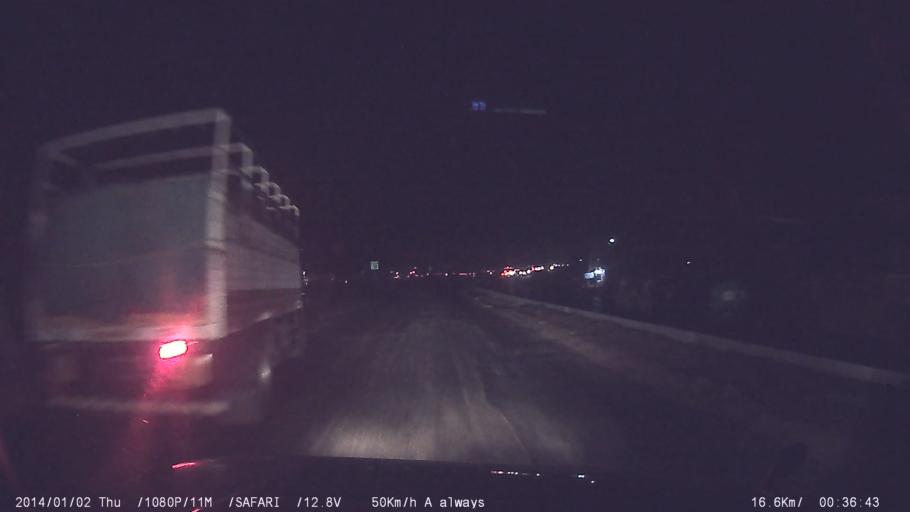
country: IN
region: Tamil Nadu
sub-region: Coimbatore
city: Madukkarai
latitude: 10.8317
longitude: 76.8312
